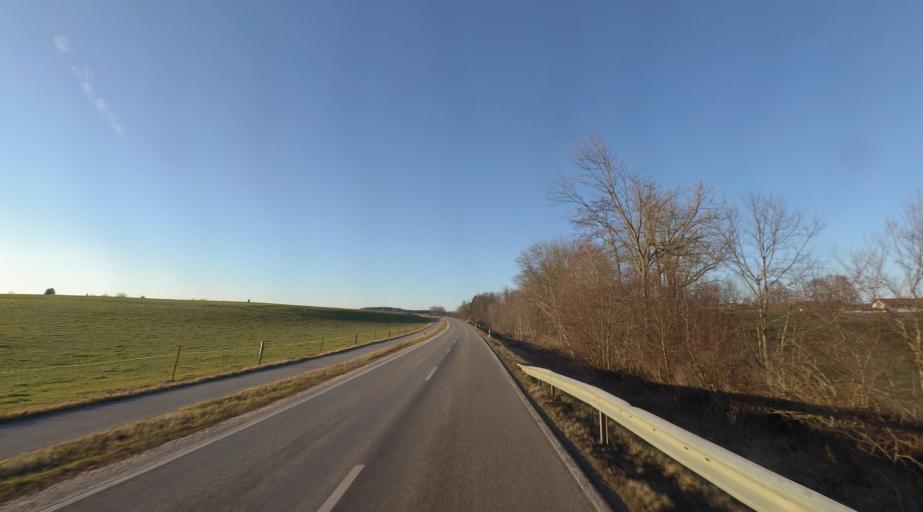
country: DE
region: Bavaria
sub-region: Upper Bavaria
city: Kirchanschoring
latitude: 47.9515
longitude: 12.7872
